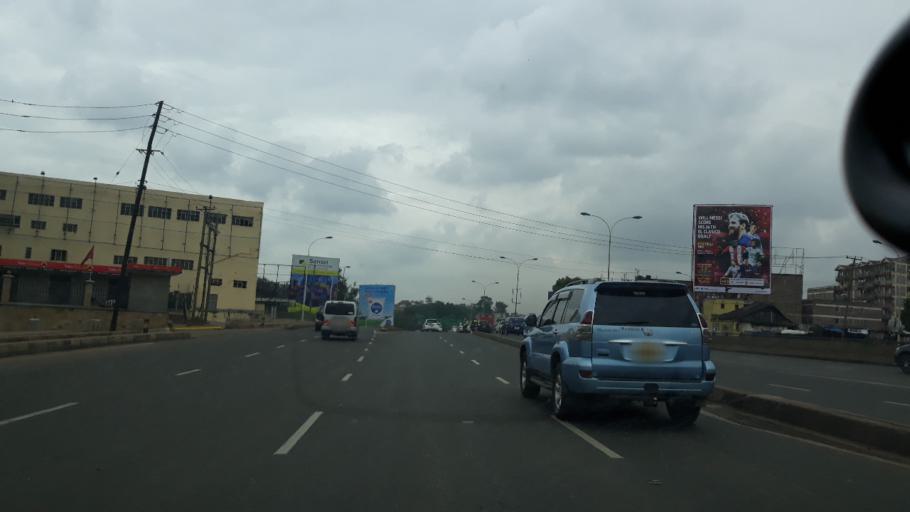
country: KE
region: Nairobi Area
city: Pumwani
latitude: -1.2663
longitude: 36.8346
